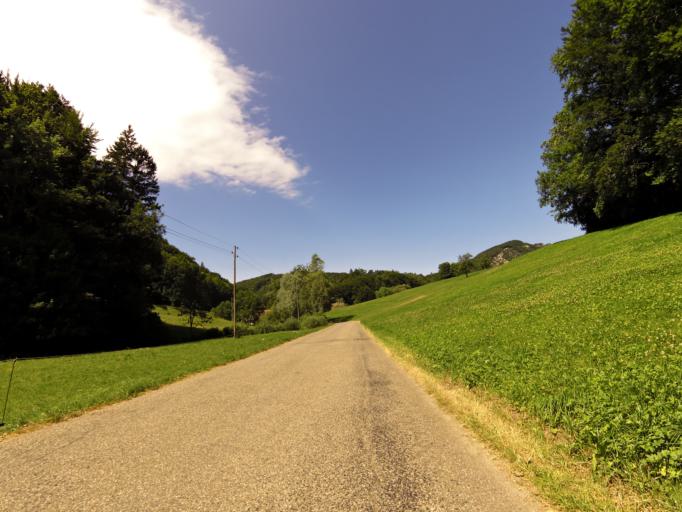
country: CH
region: Basel-Landschaft
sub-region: Bezirk Waldenburg
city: Langenbruck
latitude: 47.3567
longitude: 7.7726
